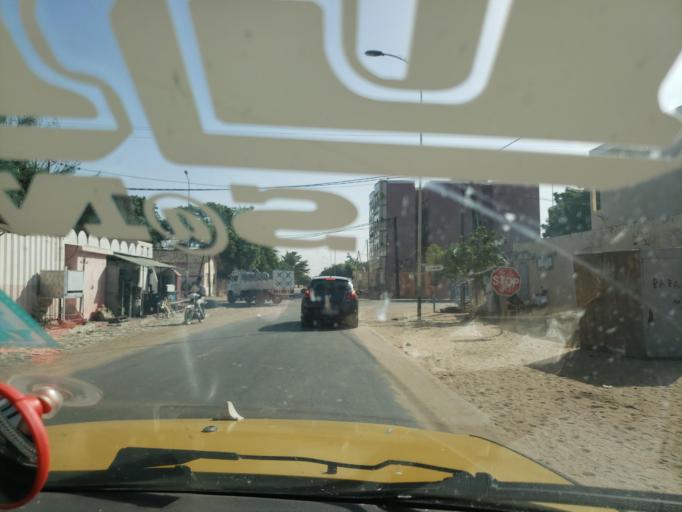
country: SN
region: Louga
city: Louga
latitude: 15.6230
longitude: -16.2142
